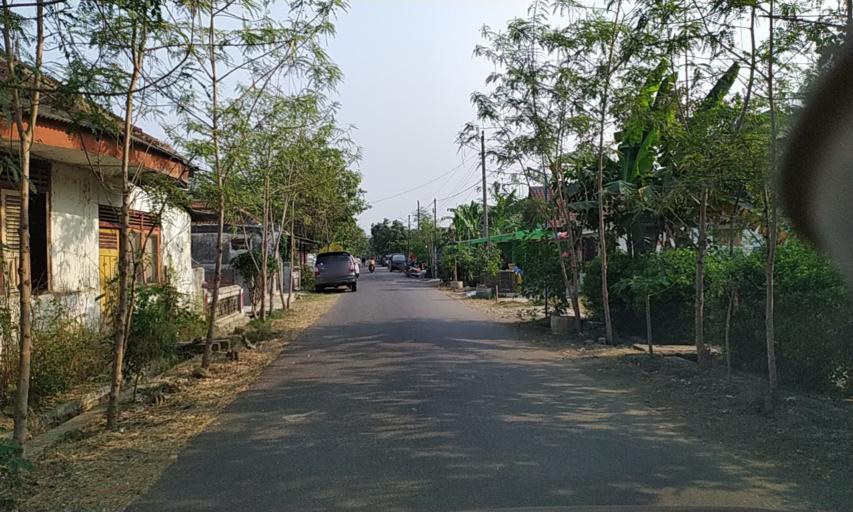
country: ID
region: Central Java
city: Sidamulya
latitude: -7.4868
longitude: 108.8073
